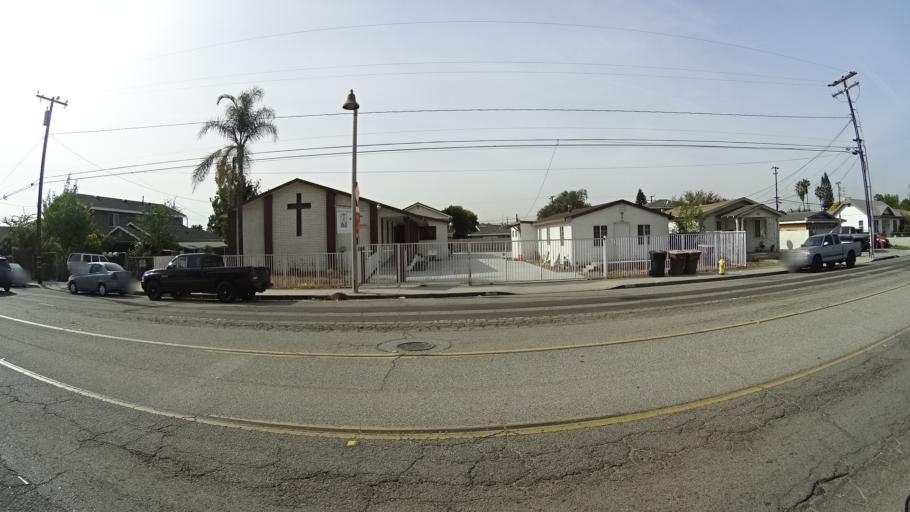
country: US
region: California
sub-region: Orange County
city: Placentia
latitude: 33.8597
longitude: -117.8739
